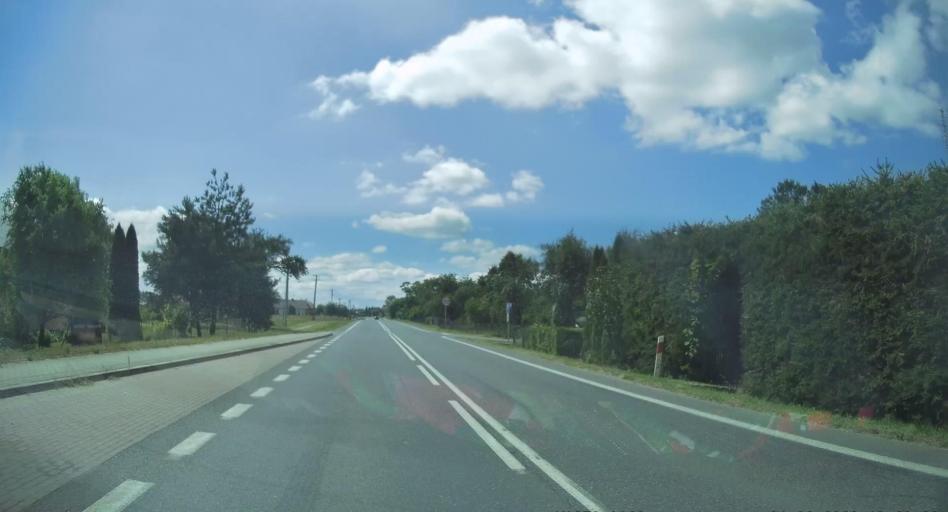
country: PL
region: Subcarpathian Voivodeship
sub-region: Powiat mielecki
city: Przeclaw
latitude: 50.1573
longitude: 21.4851
